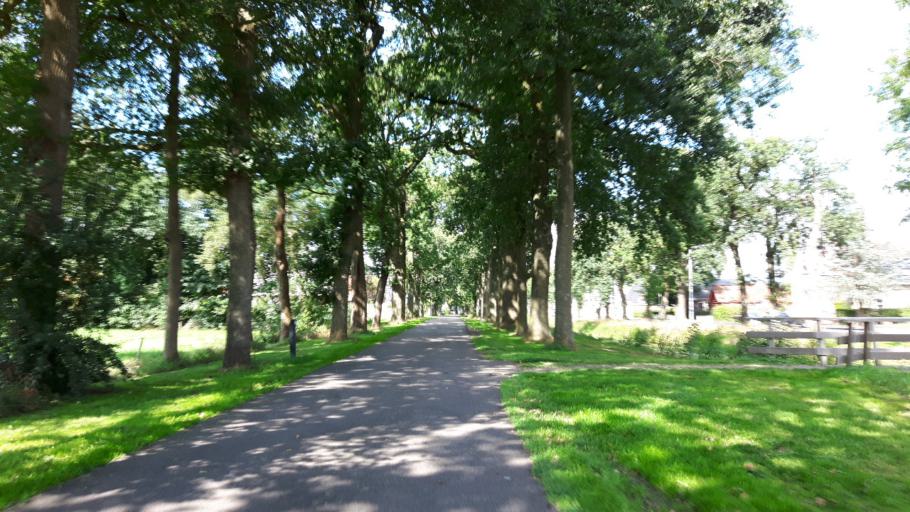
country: NL
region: Friesland
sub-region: Gemeente Smallingerland
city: Drachtstercompagnie
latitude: 53.0783
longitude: 6.2590
